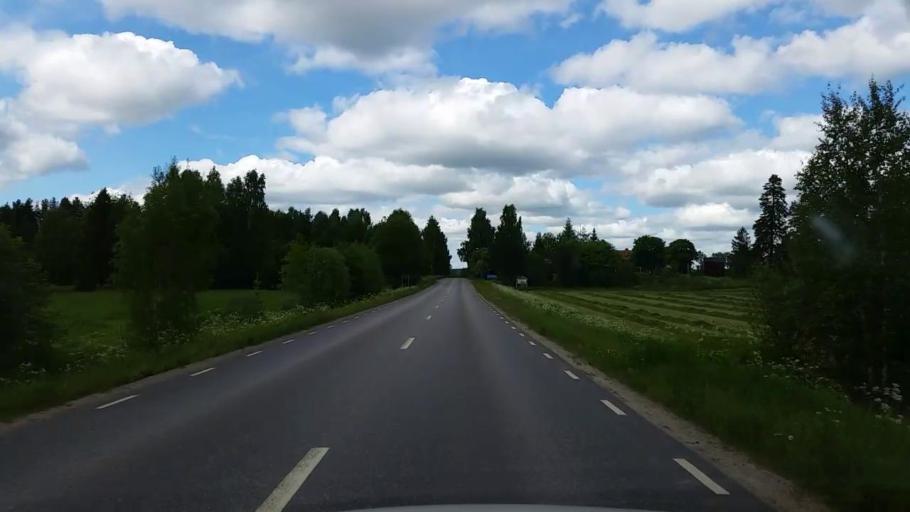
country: SE
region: Gaevleborg
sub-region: Ovanakers Kommun
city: Alfta
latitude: 61.3842
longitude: 16.0495
